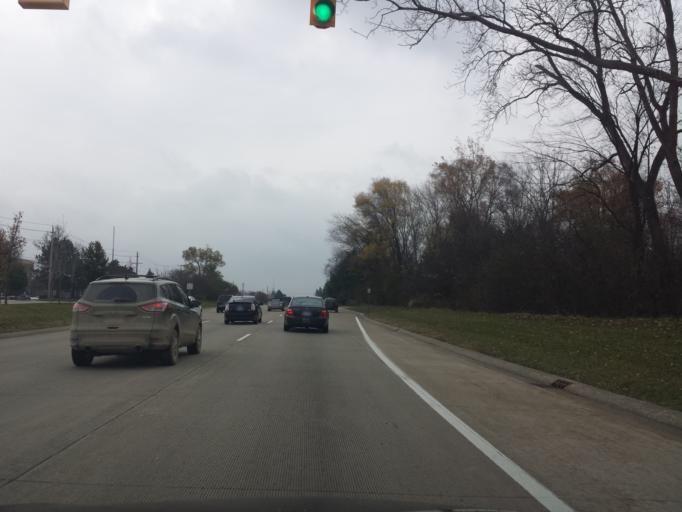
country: US
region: Michigan
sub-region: Oakland County
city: Bingham Farms
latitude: 42.5114
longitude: -83.2858
